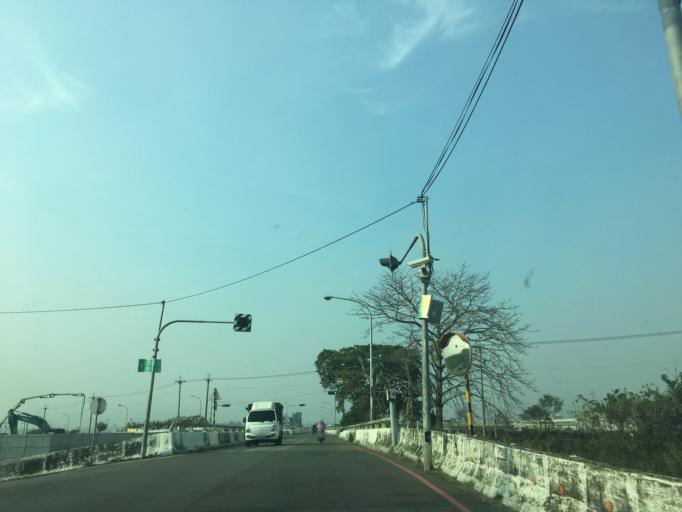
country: TW
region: Taiwan
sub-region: Taichung City
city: Taichung
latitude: 24.0701
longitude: 120.6800
